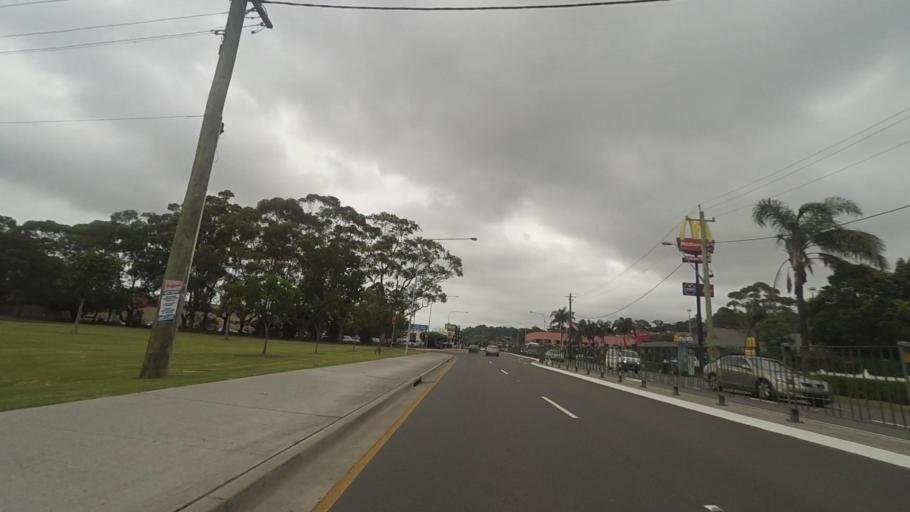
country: AU
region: New South Wales
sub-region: Wollongong
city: Mangerton
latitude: -34.4343
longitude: 150.8630
